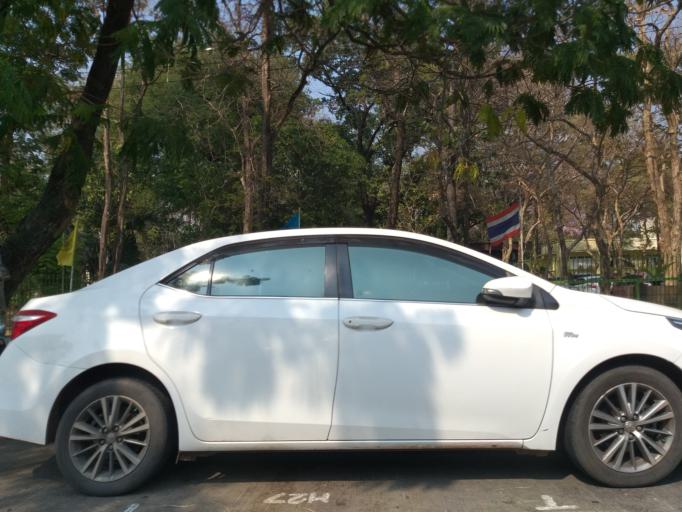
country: TH
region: Khon Kaen
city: Khon Kaen
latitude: 16.4406
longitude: 102.8336
